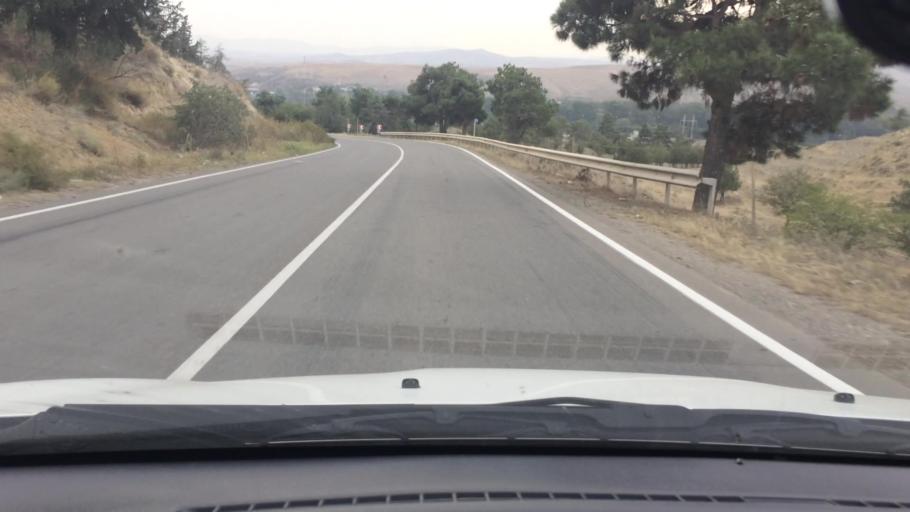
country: GE
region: Kvemo Kartli
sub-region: Gardabani
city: Gardabani
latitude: 41.3452
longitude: 45.0681
